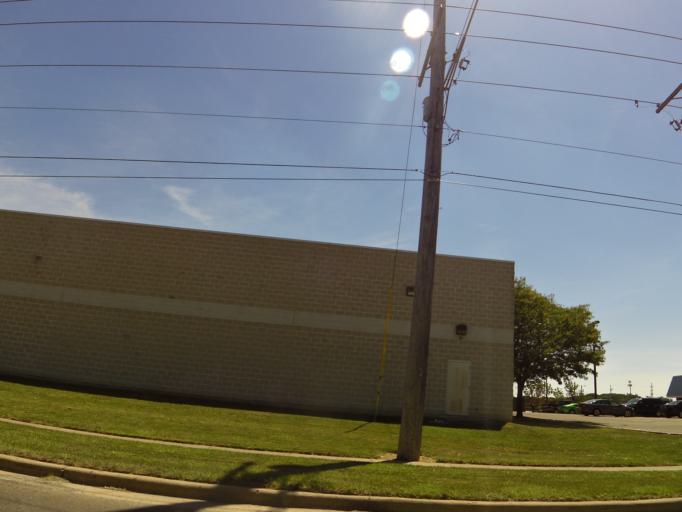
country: US
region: Illinois
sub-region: Vermilion County
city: Danville
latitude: 40.1769
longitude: -87.6299
